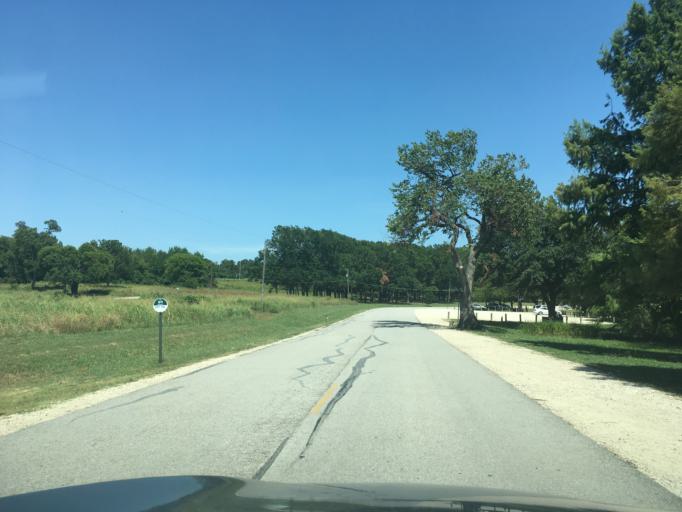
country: US
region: Texas
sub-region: Dallas County
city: Highland Park
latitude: 32.8506
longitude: -96.7205
